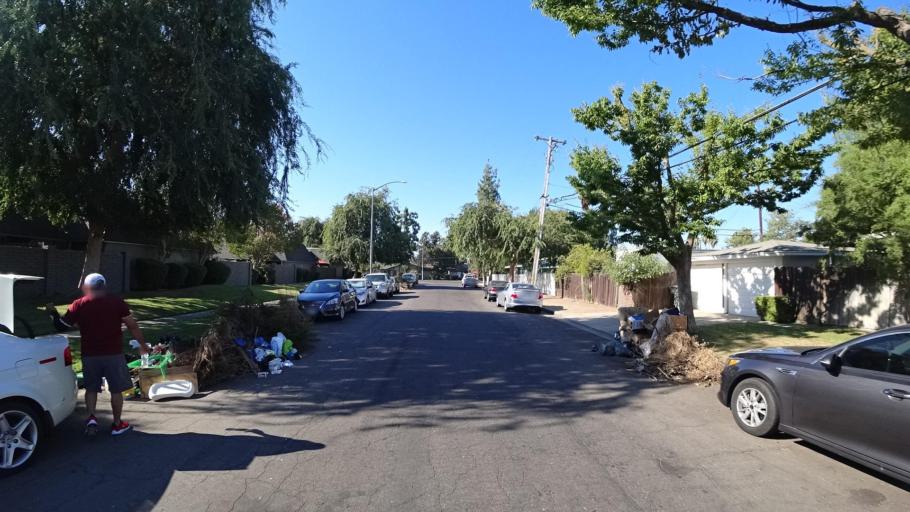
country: US
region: California
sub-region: Fresno County
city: Fresno
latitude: 36.7876
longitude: -119.7690
